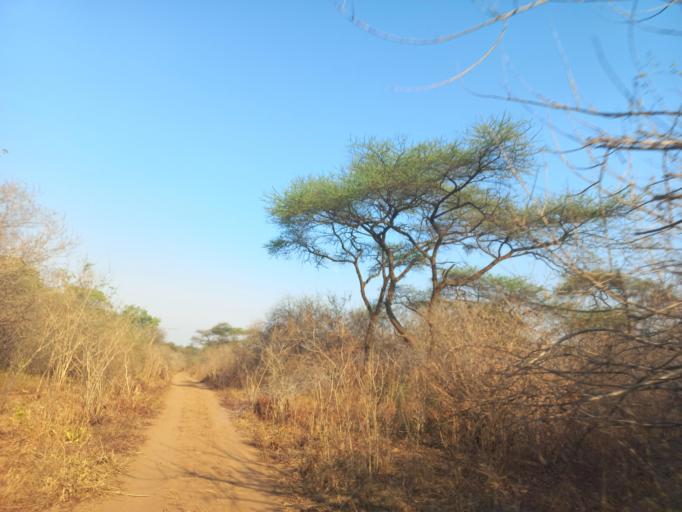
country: ZM
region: Lusaka
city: Luangwa
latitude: -15.4175
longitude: 30.2492
